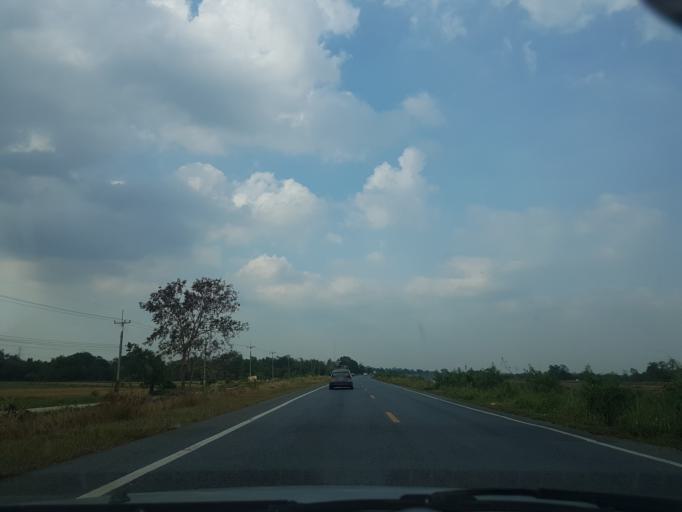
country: TH
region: Phra Nakhon Si Ayutthaya
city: Phachi
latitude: 14.4856
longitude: 100.7388
